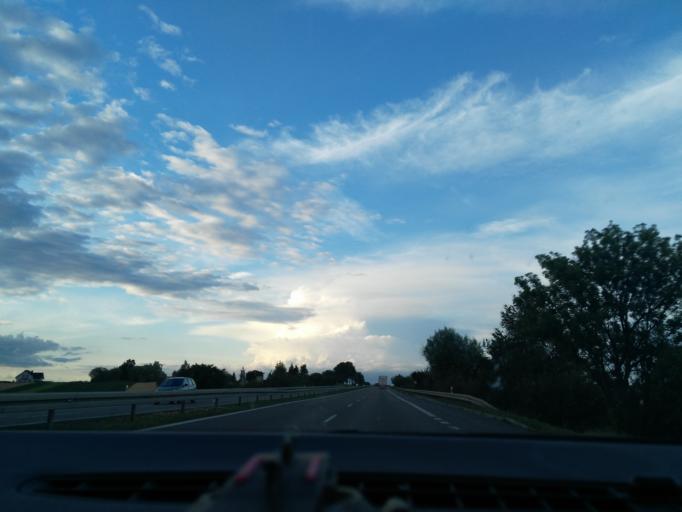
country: PL
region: Lublin Voivodeship
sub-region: Powiat lubelski
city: Niemce
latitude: 51.3247
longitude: 22.6109
